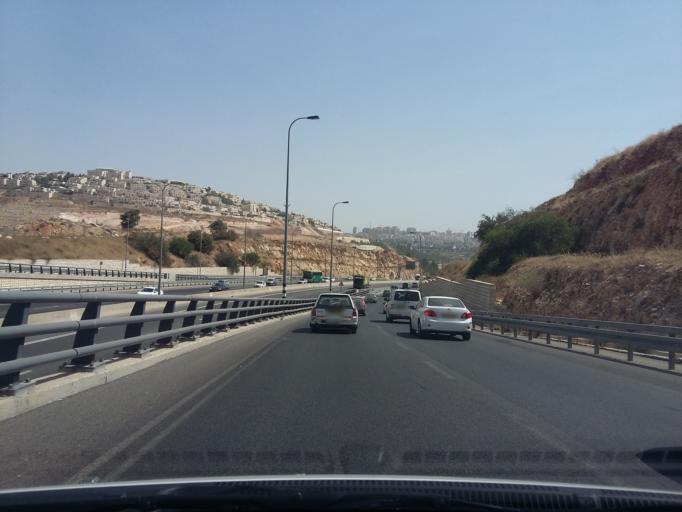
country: PS
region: West Bank
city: Bir Nabala
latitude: 31.8234
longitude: 35.2142
